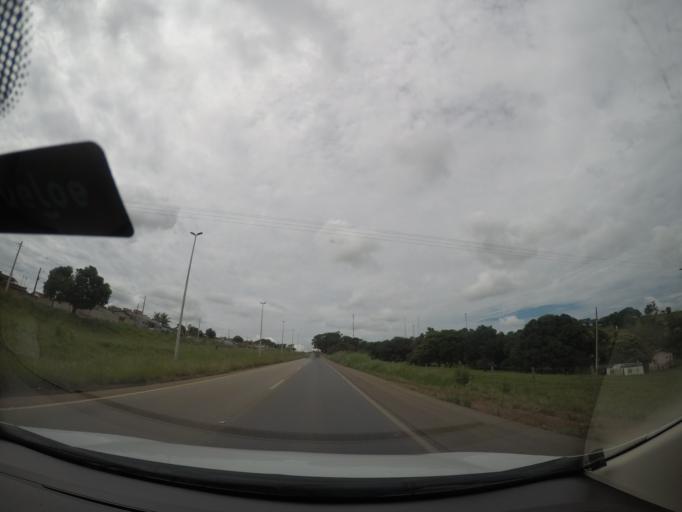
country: BR
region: Goias
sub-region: Inhumas
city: Inhumas
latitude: -16.3775
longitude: -49.5006
